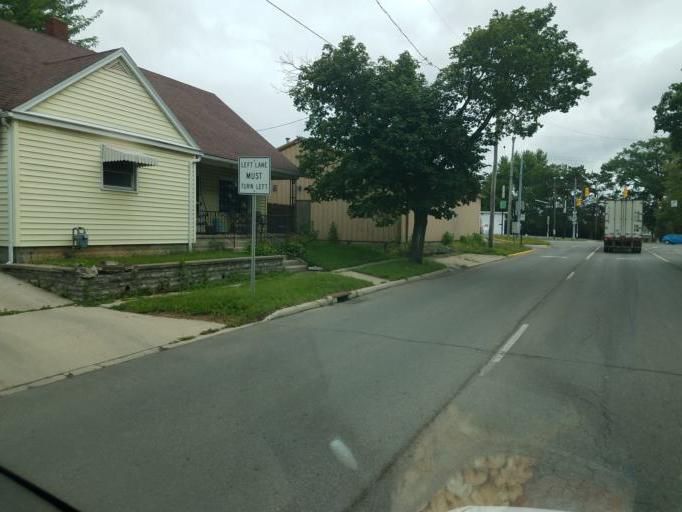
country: US
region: Ohio
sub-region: Marion County
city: Marion
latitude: 40.5791
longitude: -83.1275
